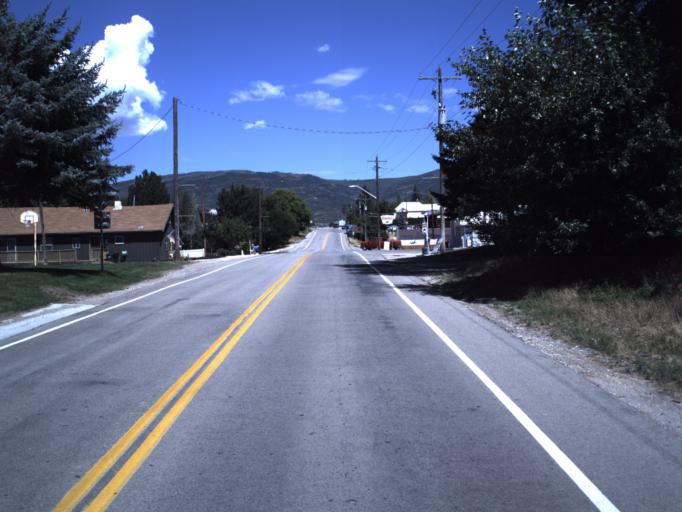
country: US
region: Utah
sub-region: Summit County
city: Oakley
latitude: 40.7139
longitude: -111.3003
